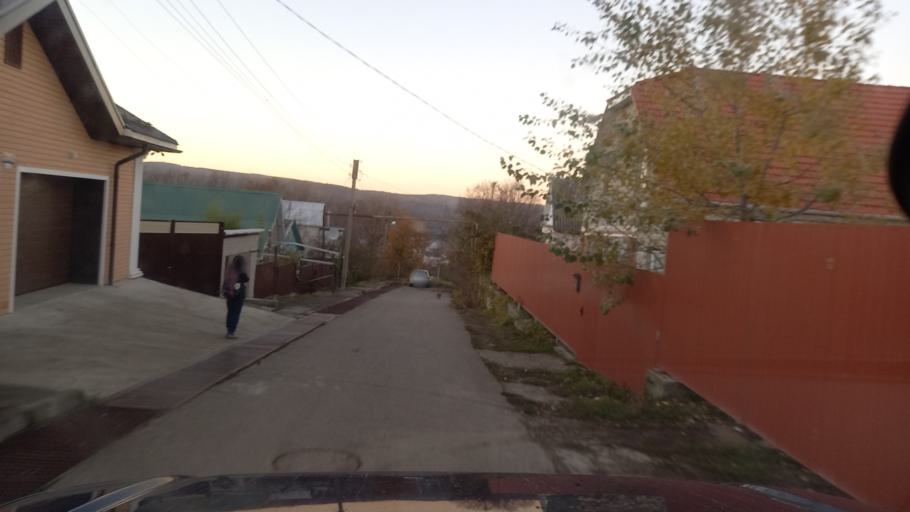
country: RU
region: Krasnodarskiy
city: Goryachiy Klyuch
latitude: 44.6223
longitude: 39.1033
